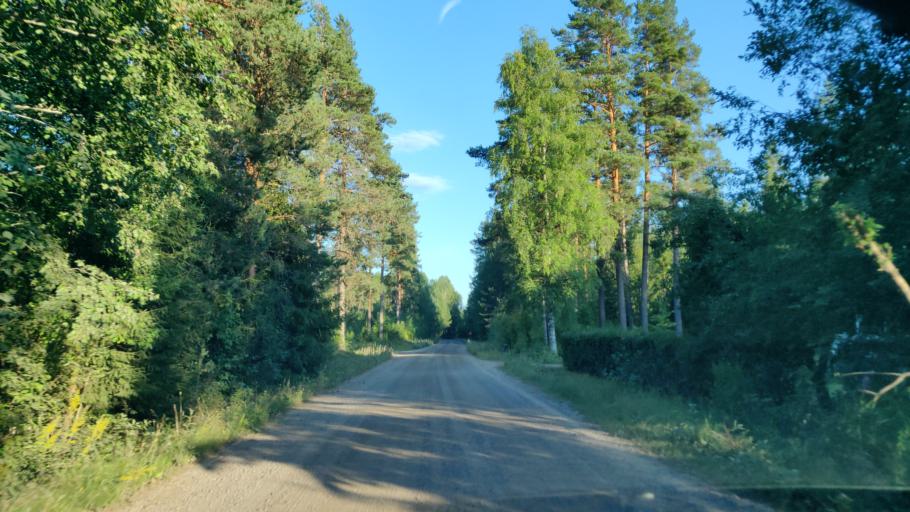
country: SE
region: Vaermland
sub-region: Hagfors Kommun
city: Ekshaerad
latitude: 60.1636
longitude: 13.5070
